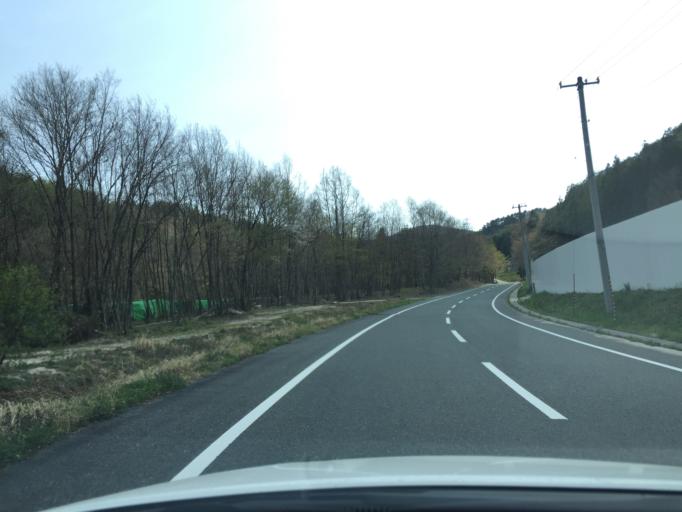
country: JP
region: Fukushima
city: Iwaki
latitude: 37.2786
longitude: 140.8388
